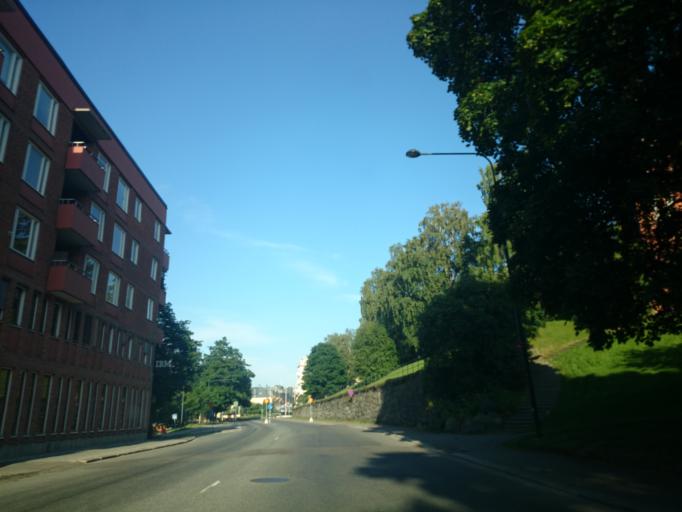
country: SE
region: Vaesternorrland
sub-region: Sundsvalls Kommun
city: Sundsvall
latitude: 62.3919
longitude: 17.2980
